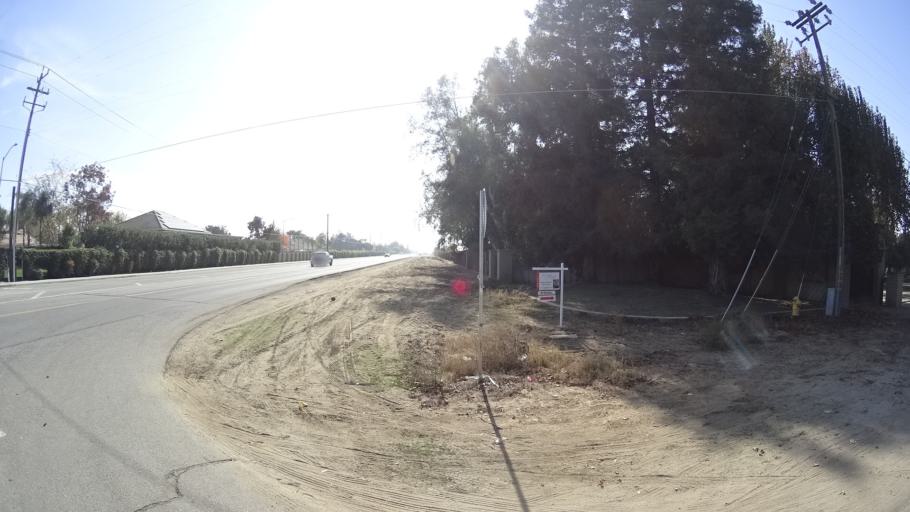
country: US
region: California
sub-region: Kern County
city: Rosedale
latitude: 35.3617
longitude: -119.1812
